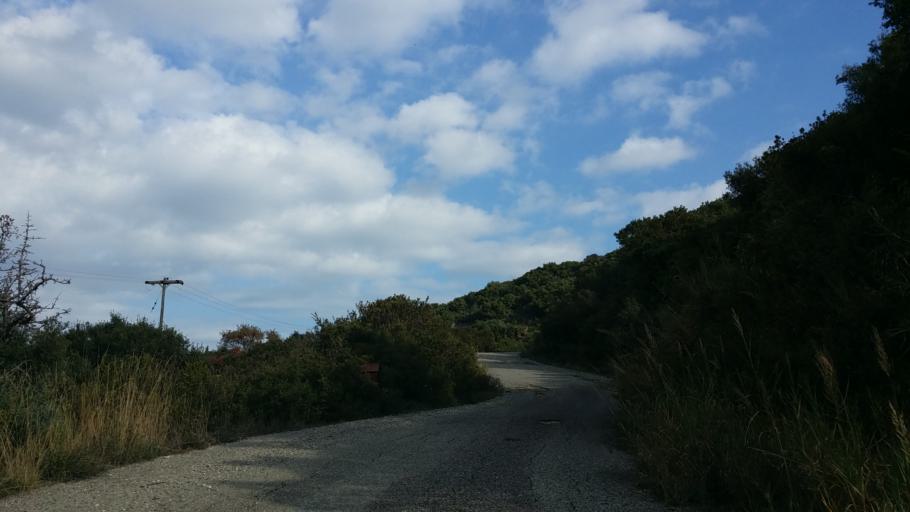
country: GR
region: West Greece
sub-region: Nomos Aitolias kai Akarnanias
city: Katouna
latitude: 38.8474
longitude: 21.0508
